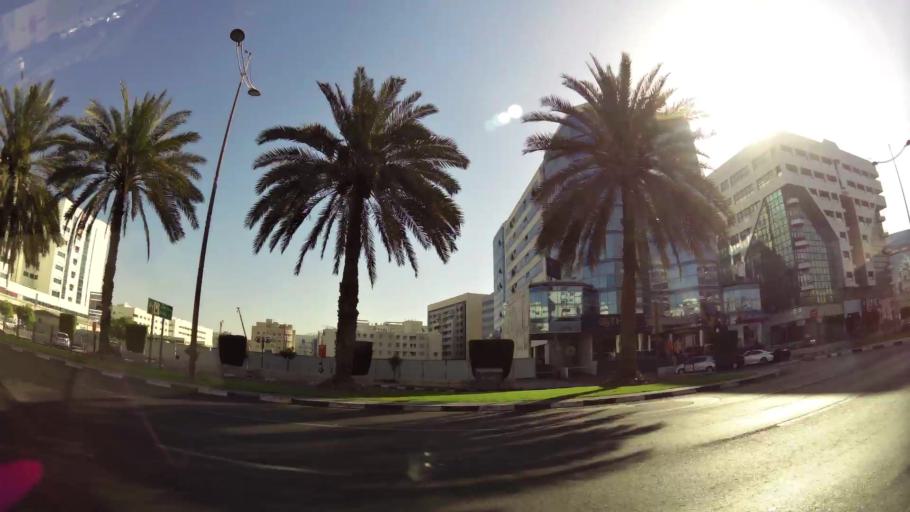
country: AE
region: Ash Shariqah
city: Sharjah
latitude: 25.2642
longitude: 55.3286
